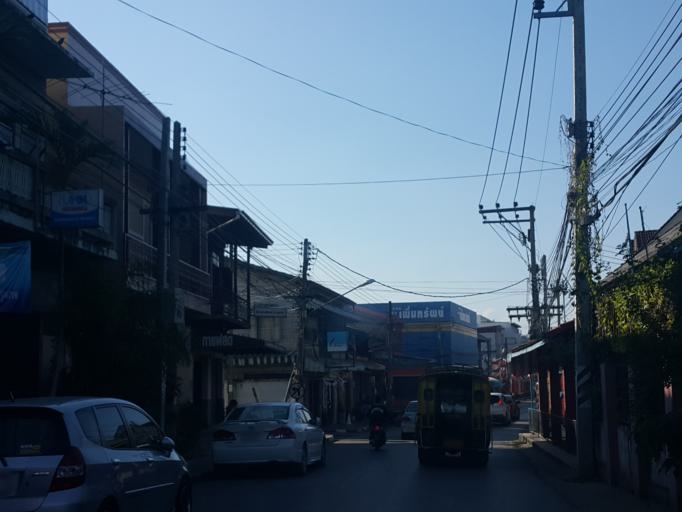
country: TH
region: Lampang
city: Lampang
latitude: 18.2899
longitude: 99.4944
